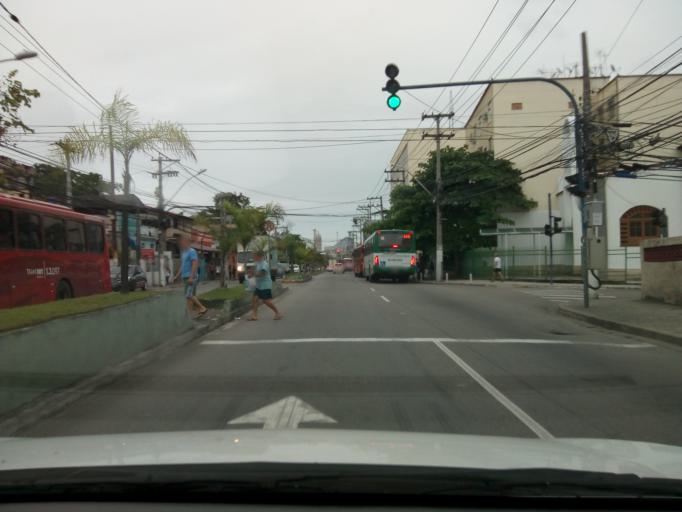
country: BR
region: Rio de Janeiro
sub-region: Niteroi
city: Niteroi
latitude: -22.8745
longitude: -43.1069
